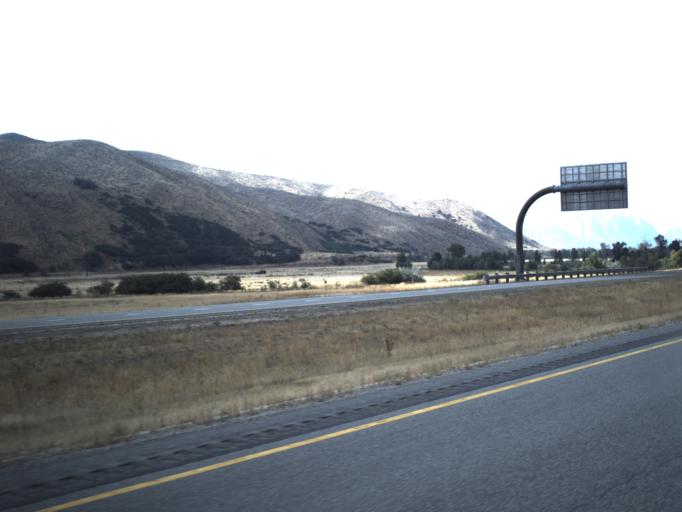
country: US
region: Utah
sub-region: Summit County
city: Coalville
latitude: 40.9758
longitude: -111.4445
